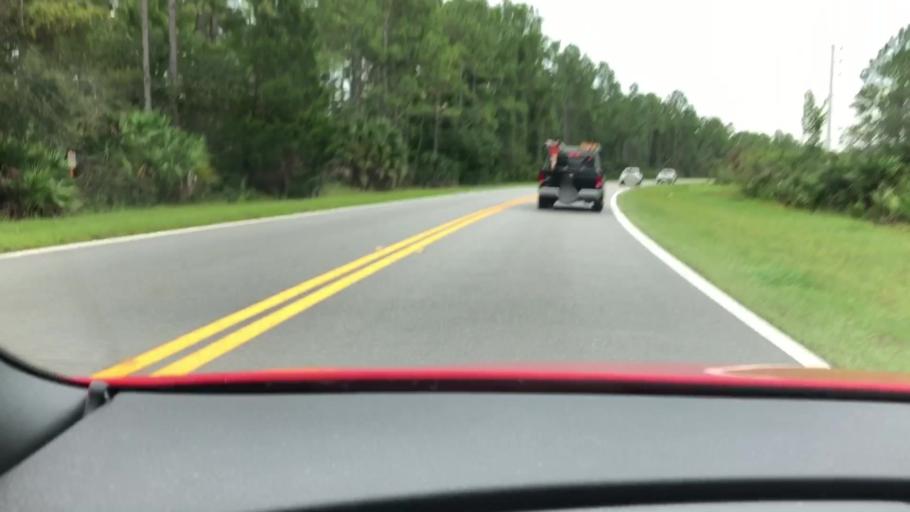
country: US
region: Florida
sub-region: Flagler County
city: Palm Coast
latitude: 29.5326
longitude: -81.2022
